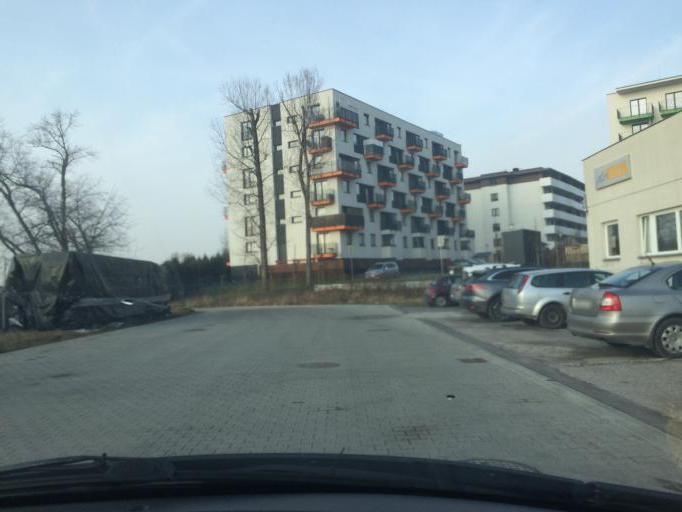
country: PL
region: Lesser Poland Voivodeship
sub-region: Powiat wielicki
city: Czarnochowice
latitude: 50.0616
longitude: 20.0153
